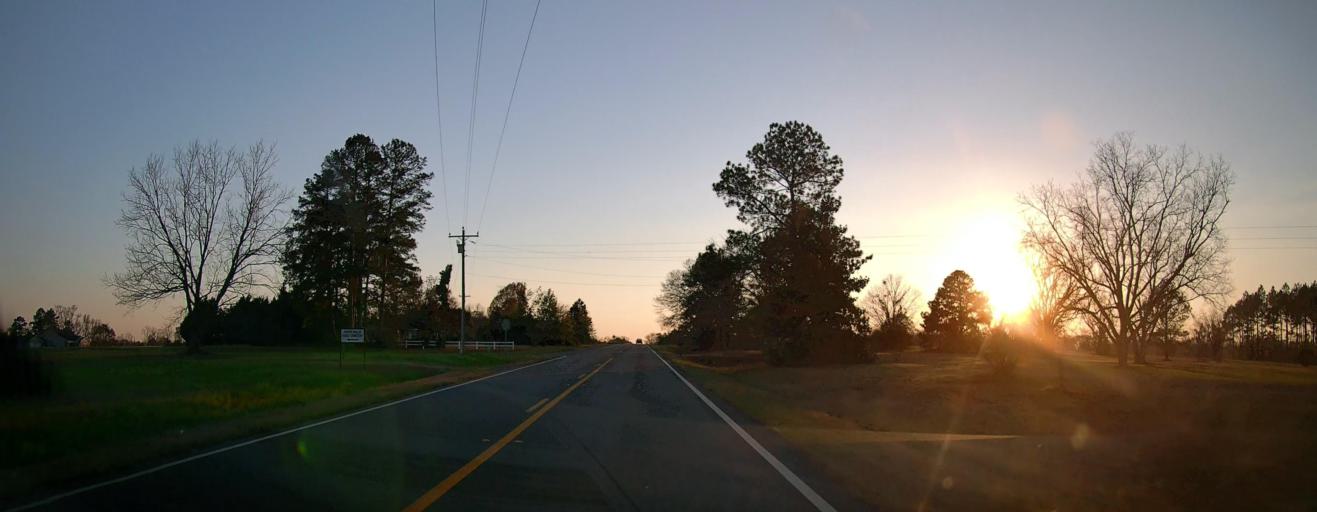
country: US
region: Georgia
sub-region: Dodge County
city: Chester
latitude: 32.3593
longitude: -83.0178
